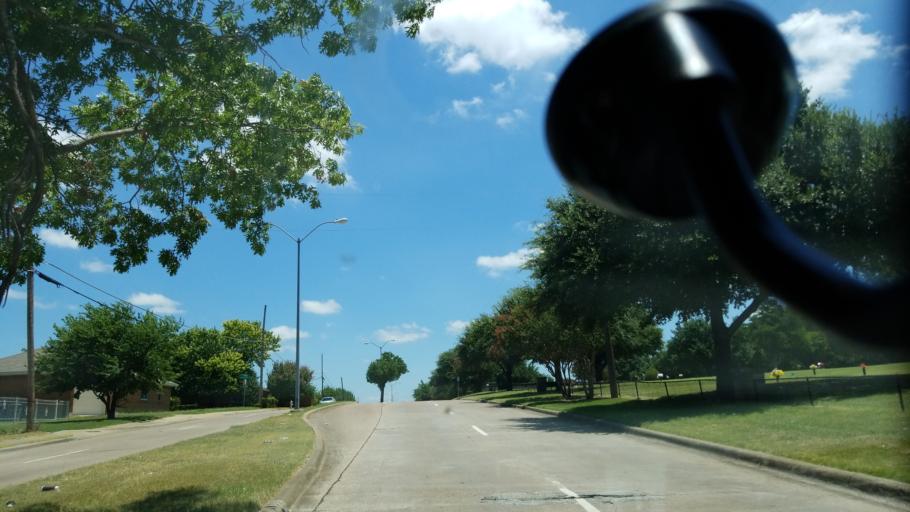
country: US
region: Texas
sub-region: Dallas County
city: Cockrell Hill
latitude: 32.6750
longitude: -96.8168
